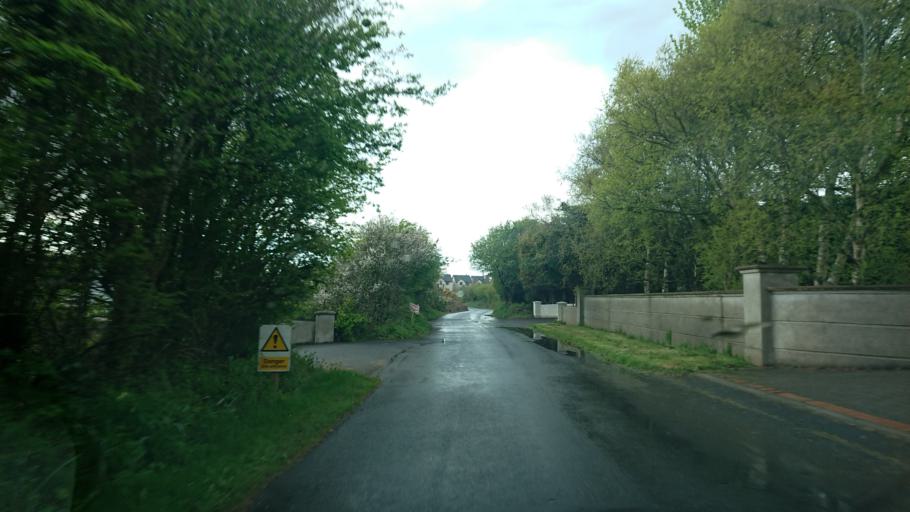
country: IE
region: Munster
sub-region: Waterford
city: Waterford
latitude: 52.2317
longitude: -7.0748
